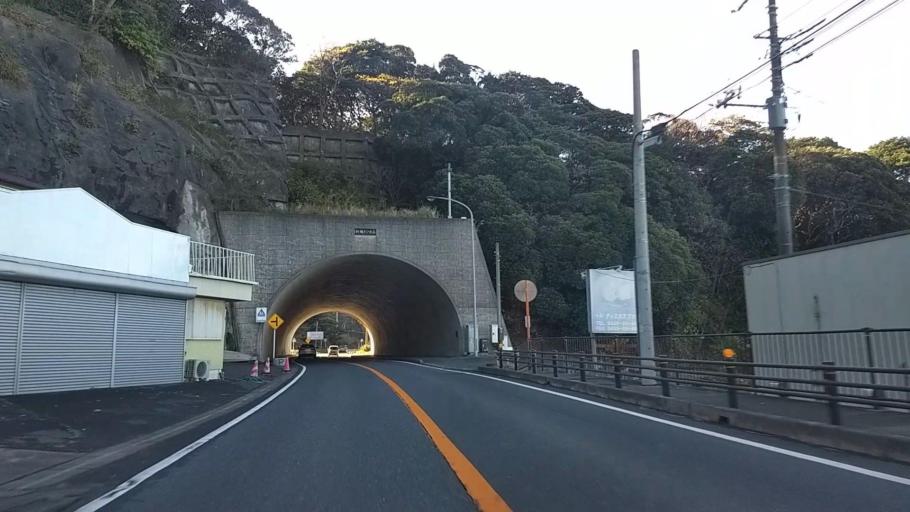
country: JP
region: Chiba
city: Futtsu
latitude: 35.1946
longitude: 139.8233
